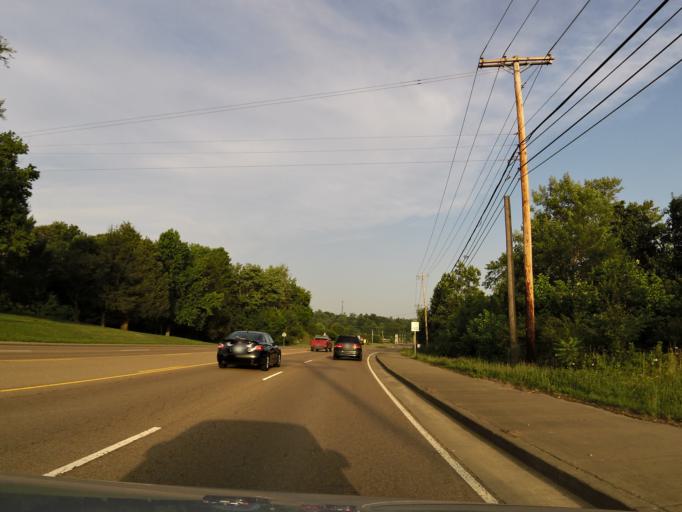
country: US
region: Tennessee
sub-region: Knox County
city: Farragut
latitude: 35.9517
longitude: -84.1198
